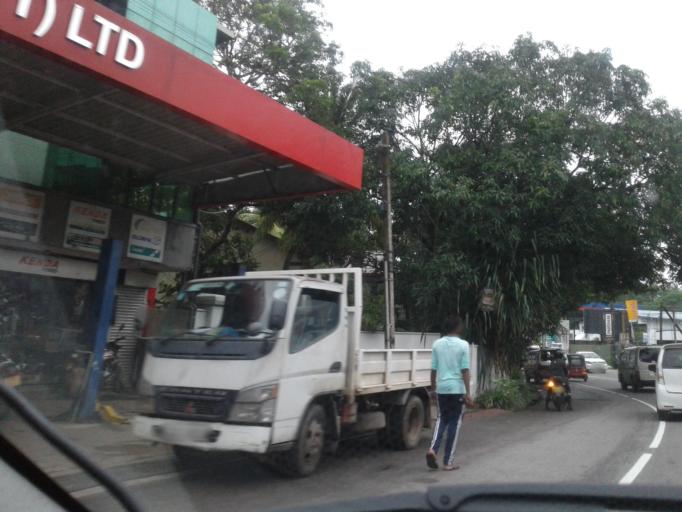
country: LK
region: Western
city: Battaramulla South
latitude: 6.9046
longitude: 79.9506
